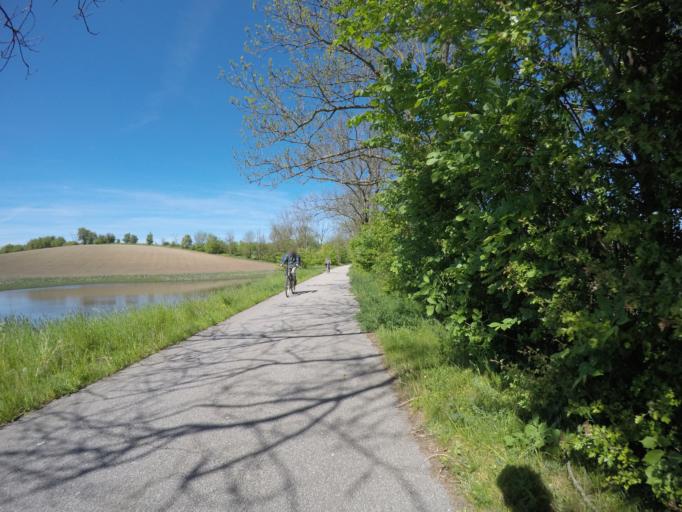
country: SE
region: Skane
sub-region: Malmo
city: Oxie
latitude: 55.5837
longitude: 13.1184
